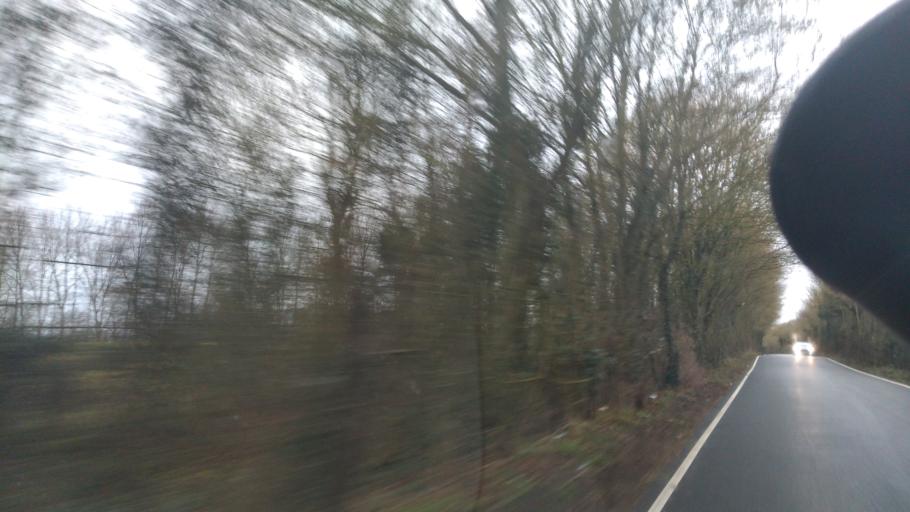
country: GB
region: England
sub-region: Oxfordshire
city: Shrivenham
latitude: 51.6164
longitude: -1.6757
